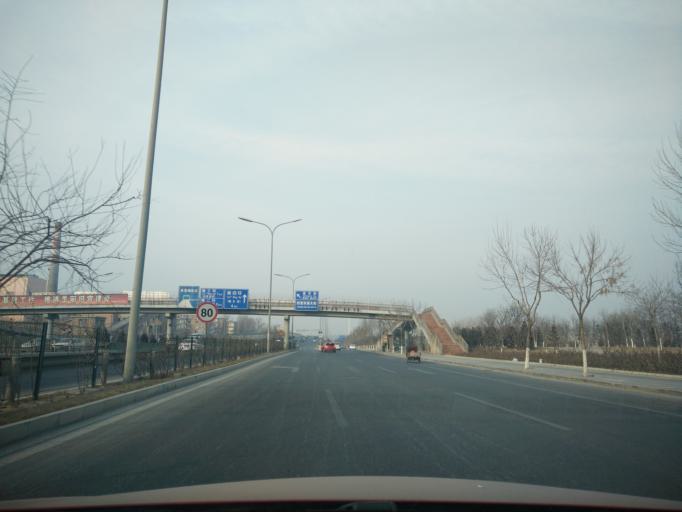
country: CN
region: Beijing
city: Jiugong
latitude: 39.7932
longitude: 116.4240
